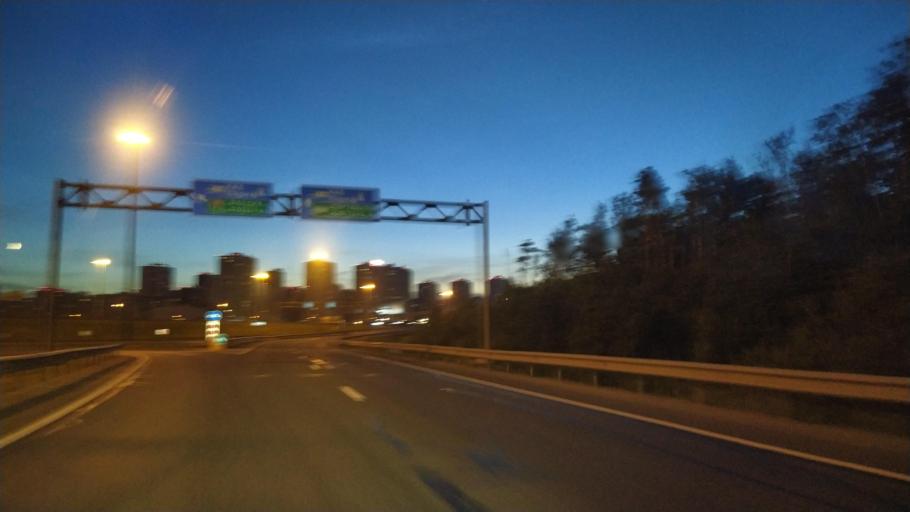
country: RU
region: Leningrad
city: Rybatskoye
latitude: 59.8944
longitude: 30.5277
